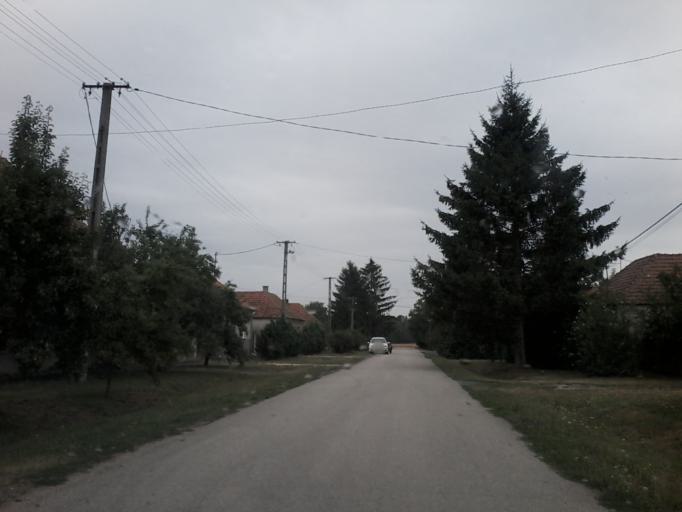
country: HU
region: Vas
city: Celldomolk
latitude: 47.2087
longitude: 17.0711
